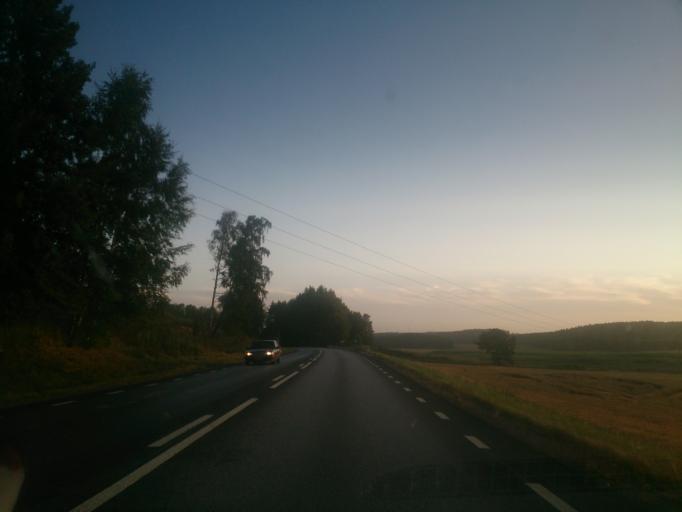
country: SE
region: Soedermanland
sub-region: Nykopings Kommun
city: Nykoping
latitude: 58.7966
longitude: 17.0816
